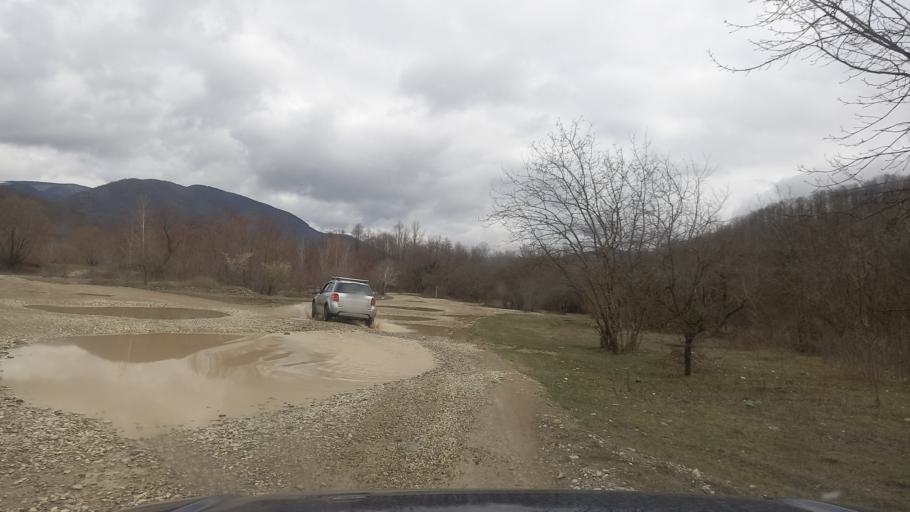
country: RU
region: Krasnodarskiy
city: Pshada
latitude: 44.4830
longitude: 38.4082
